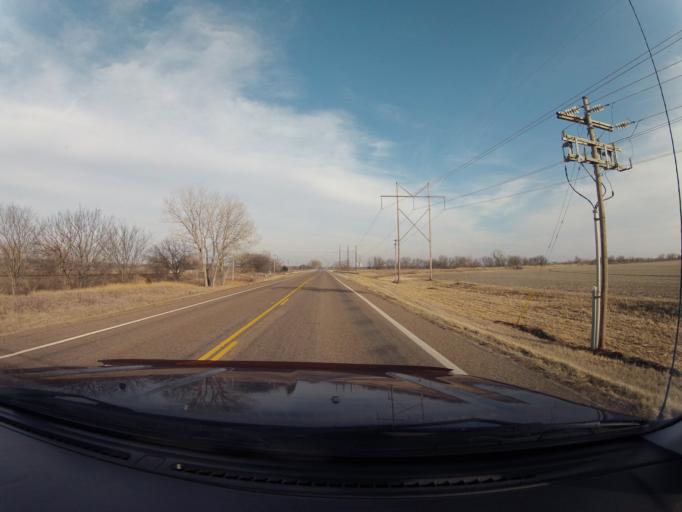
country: US
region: Kansas
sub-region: Pottawatomie County
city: Saint Marys
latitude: 39.2164
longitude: -96.1702
